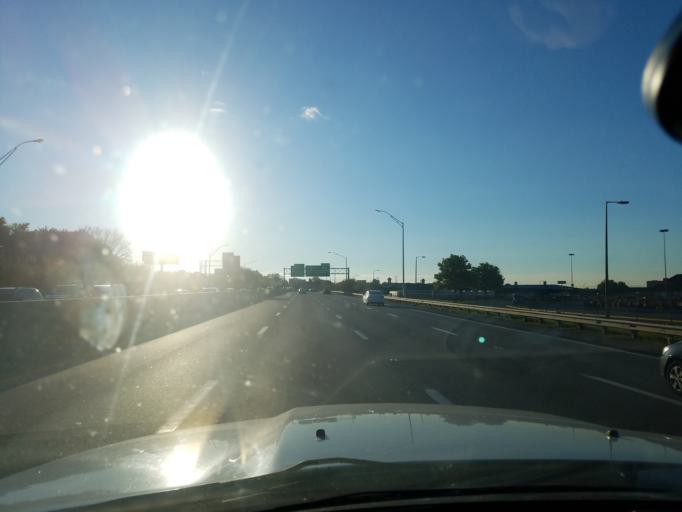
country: US
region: Kentucky
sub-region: Jefferson County
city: Audubon Park
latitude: 38.2044
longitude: -85.7412
